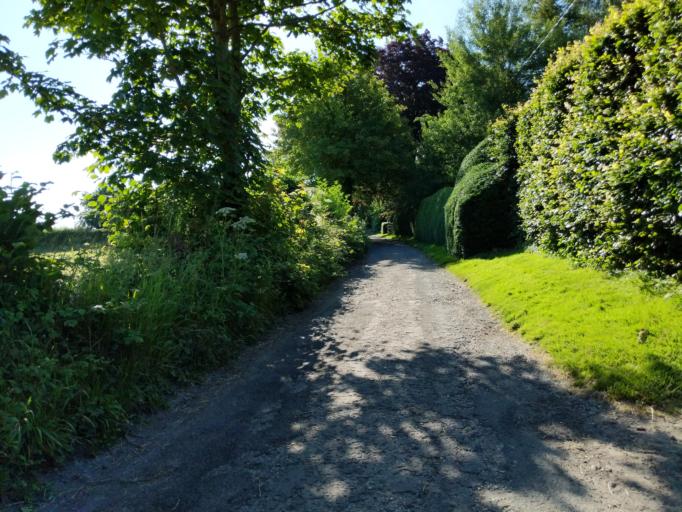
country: GB
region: England
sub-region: Kent
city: Faversham
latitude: 51.3269
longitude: 0.9360
